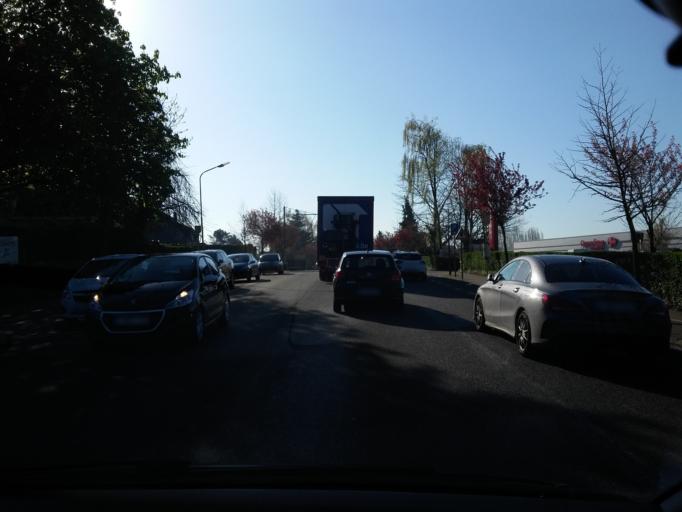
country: BE
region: Wallonia
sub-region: Province du Brabant Wallon
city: Waterloo
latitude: 50.7112
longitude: 4.4019
